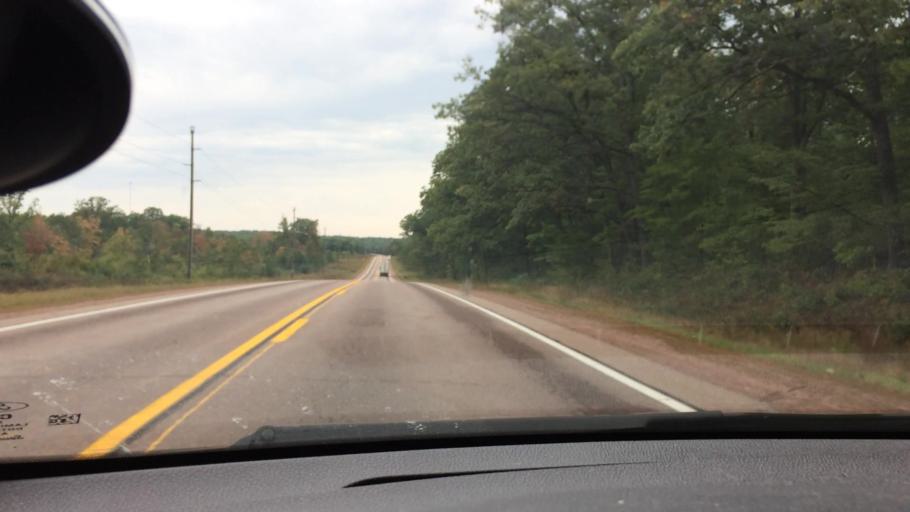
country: US
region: Wisconsin
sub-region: Clark County
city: Neillsville
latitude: 44.5865
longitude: -90.7516
